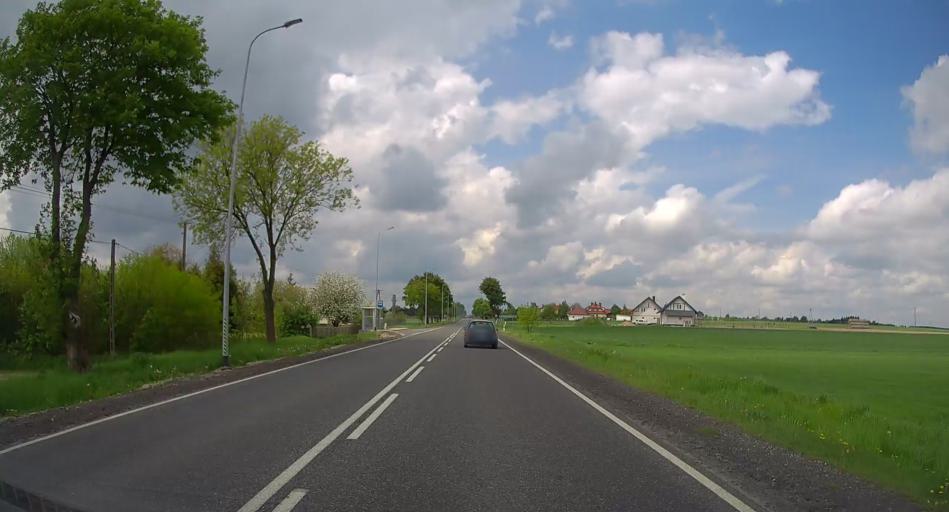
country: PL
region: Masovian Voivodeship
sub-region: Powiat plonski
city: Zaluski
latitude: 52.4428
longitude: 20.5377
